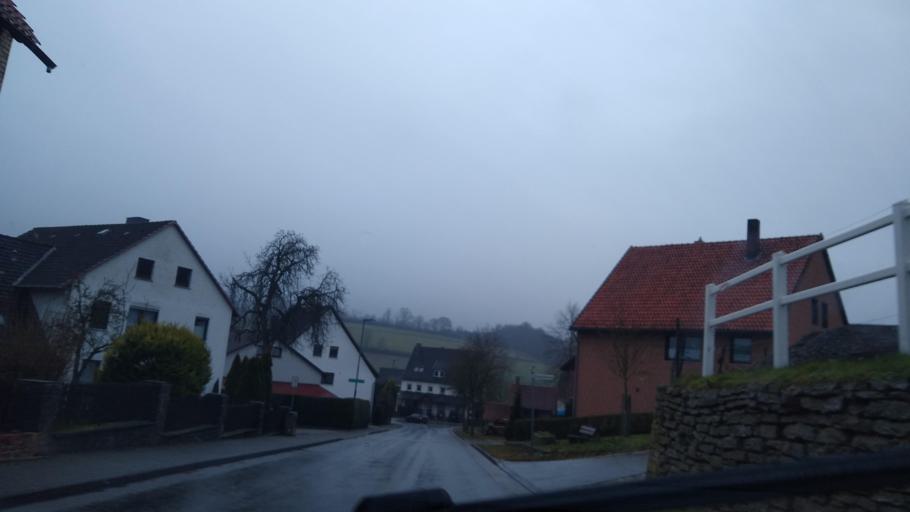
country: DE
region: Lower Saxony
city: Vahlbruch
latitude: 51.9091
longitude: 9.3230
